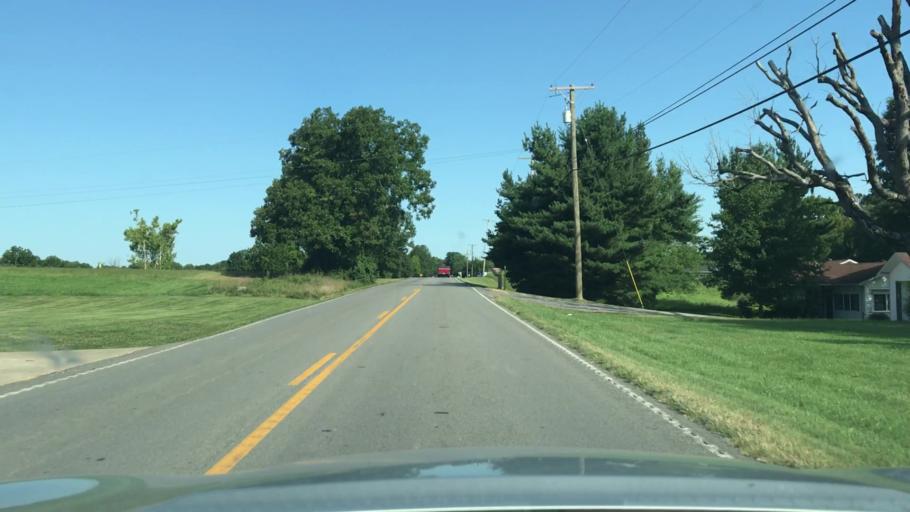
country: US
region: Kentucky
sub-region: Muhlenberg County
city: Greenville
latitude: 37.1836
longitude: -87.1577
